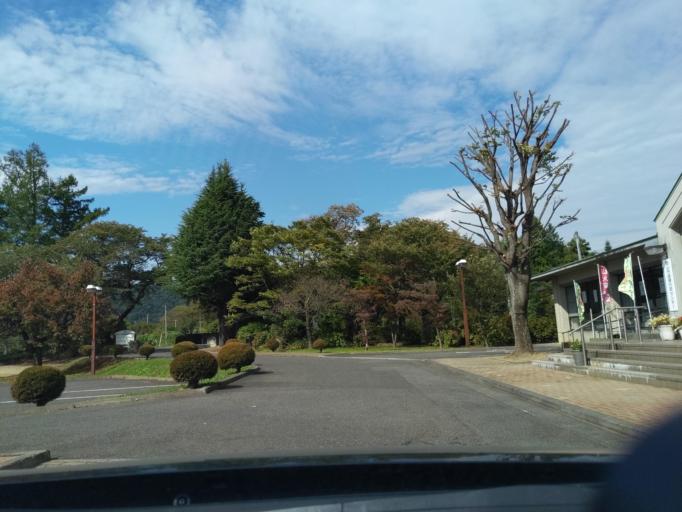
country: JP
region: Fukushima
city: Koriyama
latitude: 37.3937
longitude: 140.2699
